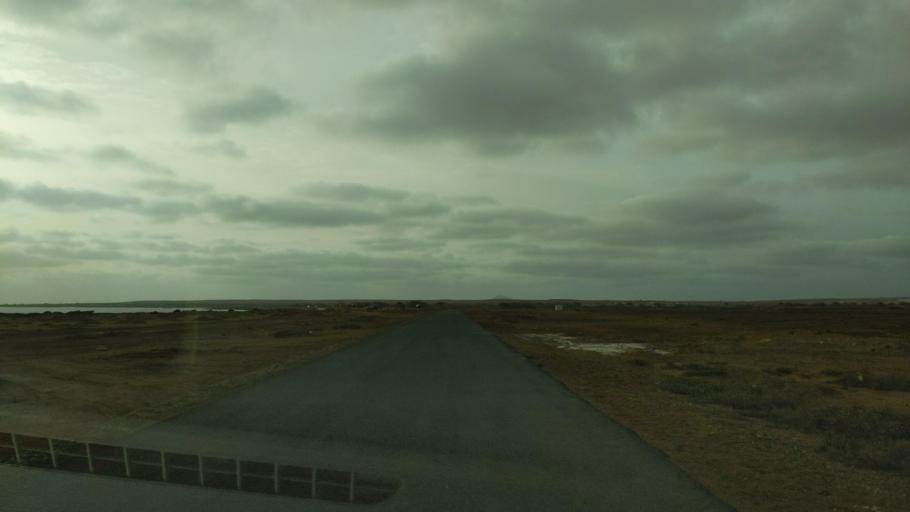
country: CV
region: Sal
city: Espargos
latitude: 16.6851
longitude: -22.9373
